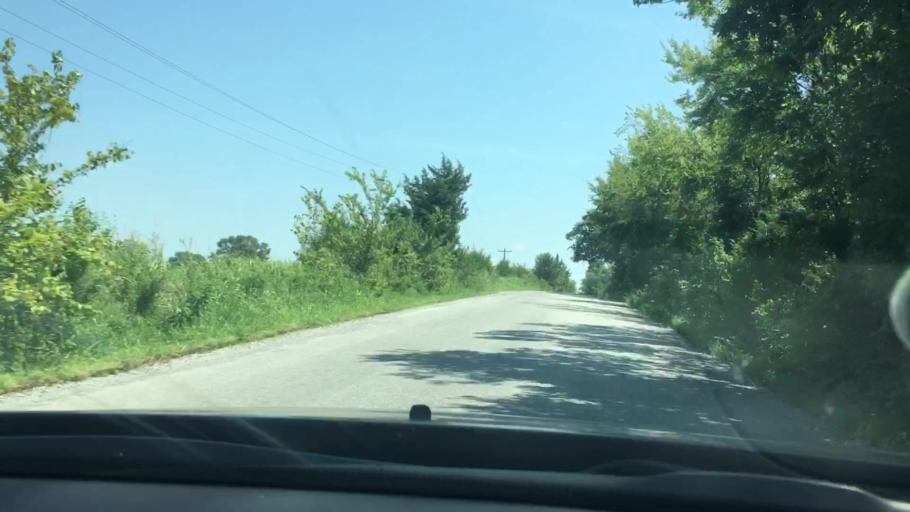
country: US
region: Oklahoma
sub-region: Bryan County
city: Durant
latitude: 34.2587
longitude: -96.3917
